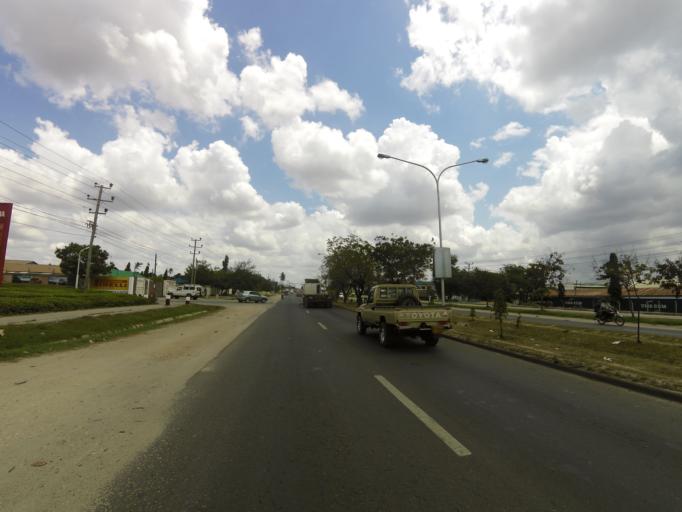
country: TZ
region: Dar es Salaam
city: Dar es Salaam
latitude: -6.8569
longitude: 39.2202
